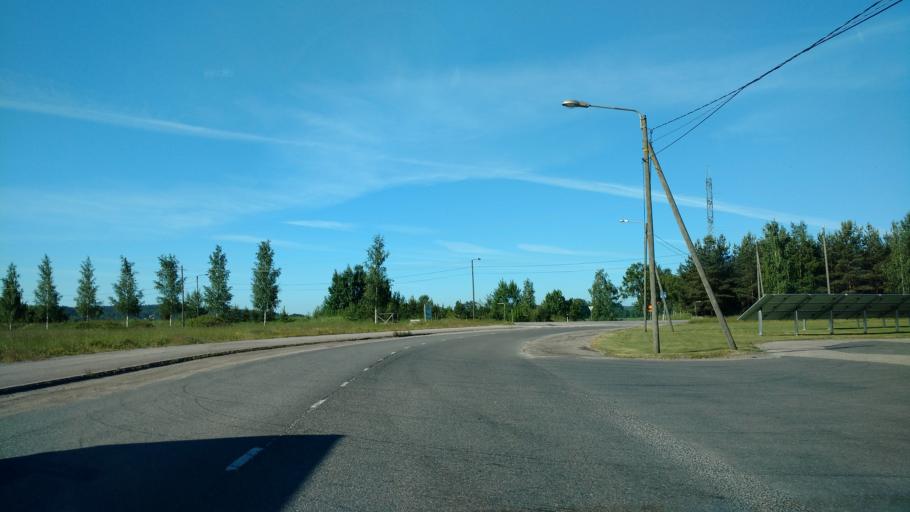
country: FI
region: Varsinais-Suomi
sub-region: Salo
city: Halikko
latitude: 60.3847
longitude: 23.1014
